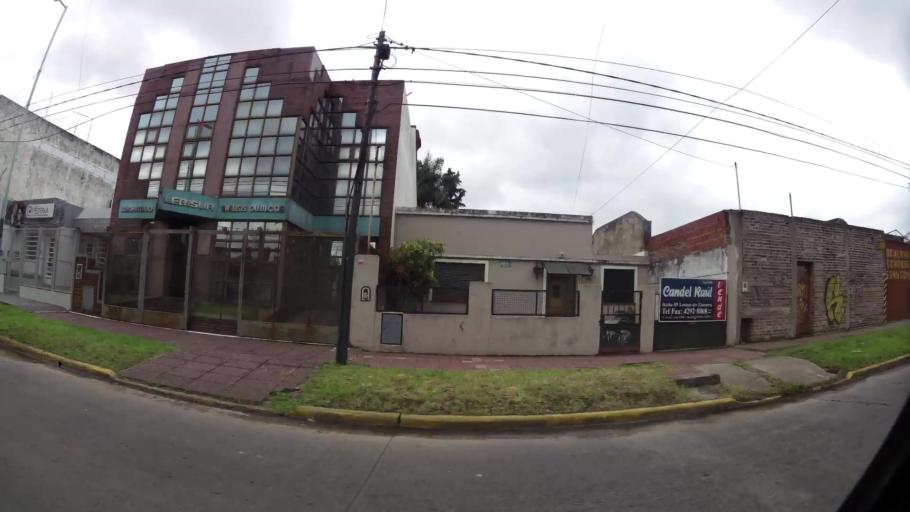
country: AR
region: Buenos Aires
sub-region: Partido de Lomas de Zamora
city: Lomas de Zamora
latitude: -34.7598
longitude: -58.3835
